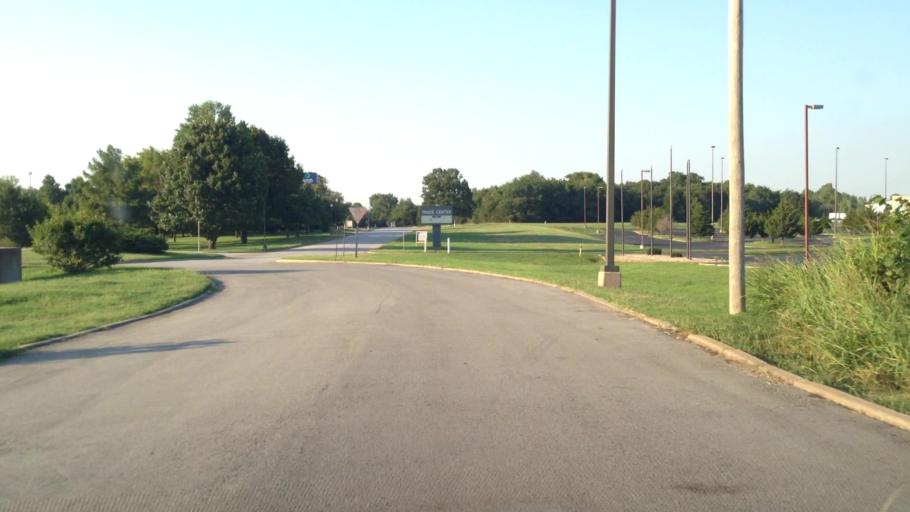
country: US
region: Missouri
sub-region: Jasper County
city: Duquesne
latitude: 37.0486
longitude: -94.4734
